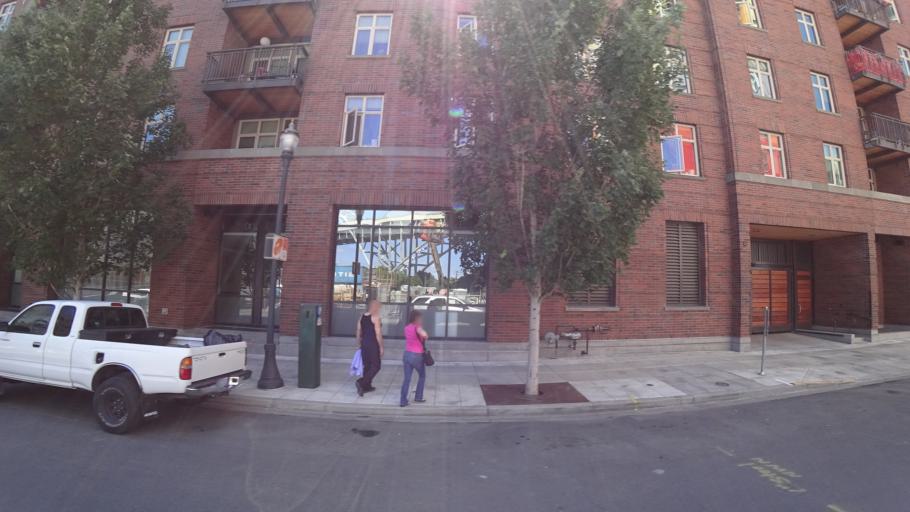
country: US
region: Oregon
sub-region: Multnomah County
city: Portland
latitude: 45.5343
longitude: -122.6850
